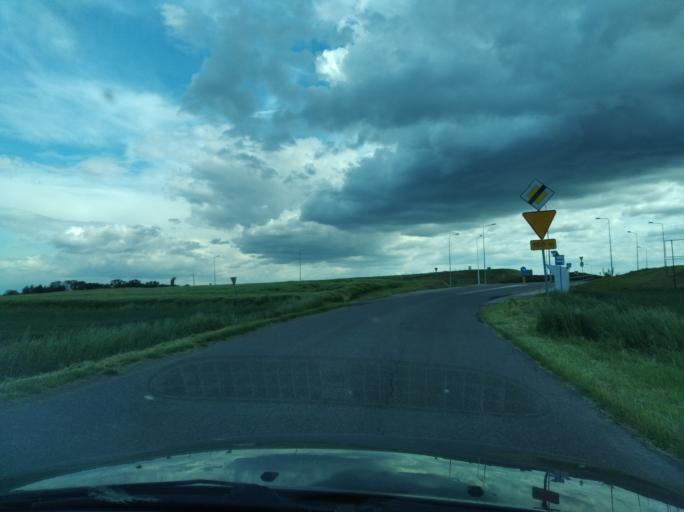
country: PL
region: Subcarpathian Voivodeship
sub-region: Powiat jaroslawski
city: Pawlosiow
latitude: 49.9483
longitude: 22.6672
